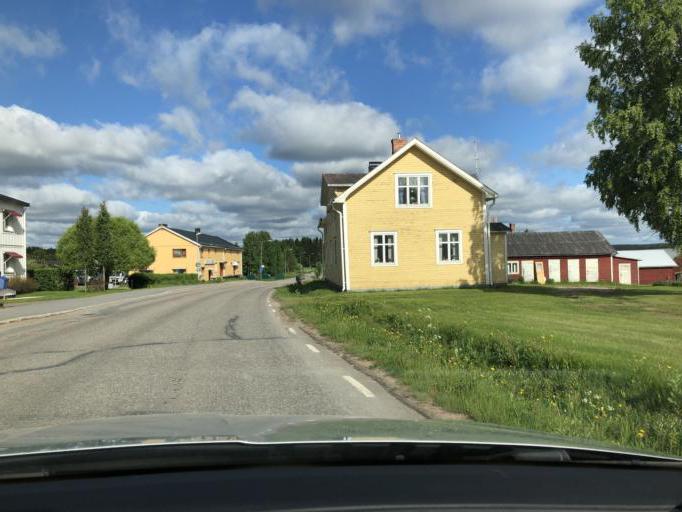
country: SE
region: Norrbotten
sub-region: Pajala Kommun
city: Pajala
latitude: 67.2174
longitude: 23.3585
